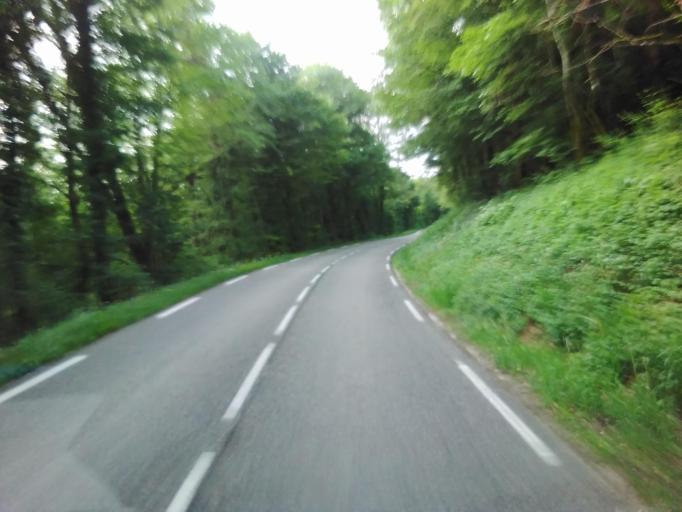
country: FR
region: Franche-Comte
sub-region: Departement du Jura
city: Arbois
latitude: 46.8957
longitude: 5.7944
